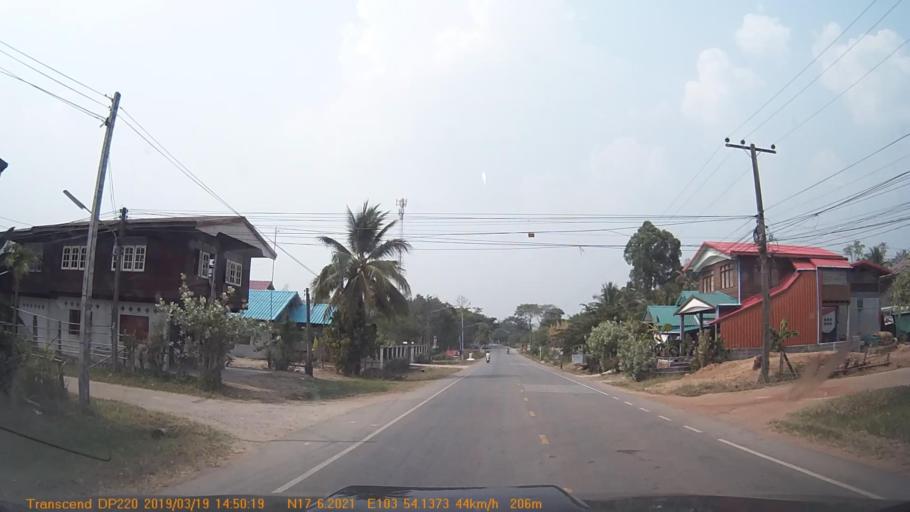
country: TH
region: Sakon Nakhon
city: Kut Bak
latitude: 17.1035
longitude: 103.9023
